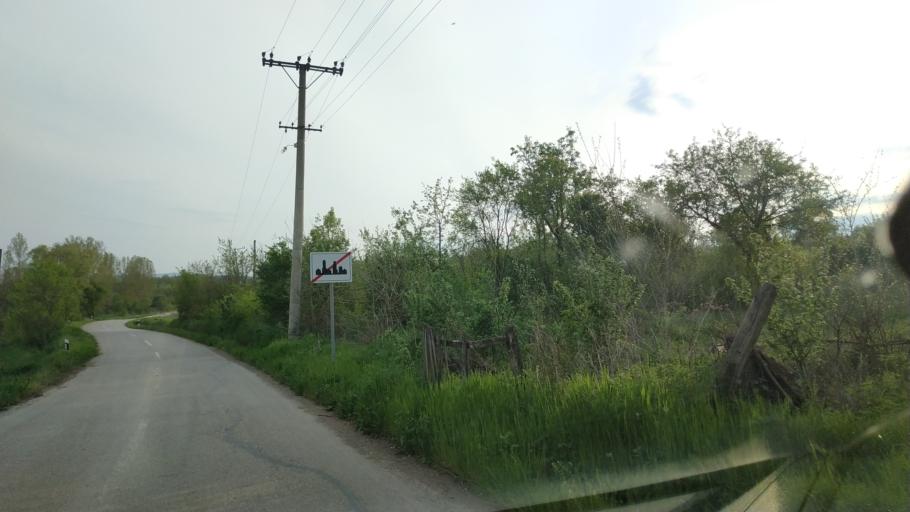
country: RS
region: Central Serbia
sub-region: Nisavski Okrug
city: Aleksinac
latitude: 43.4936
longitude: 21.8204
